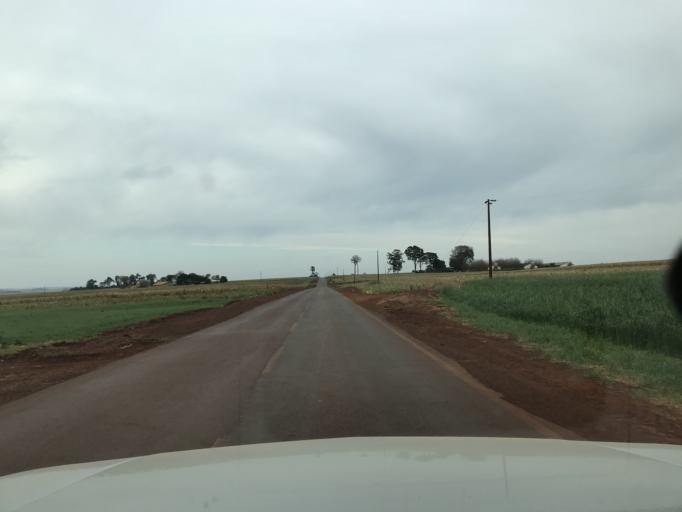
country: BR
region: Parana
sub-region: Palotina
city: Palotina
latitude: -24.4201
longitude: -53.8884
